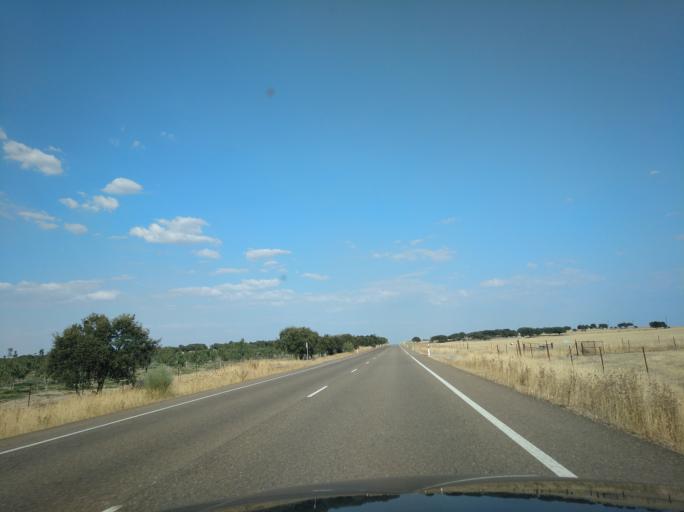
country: ES
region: Extremadura
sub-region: Provincia de Badajoz
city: Villanueva del Fresno
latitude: 38.3797
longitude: -7.2337
